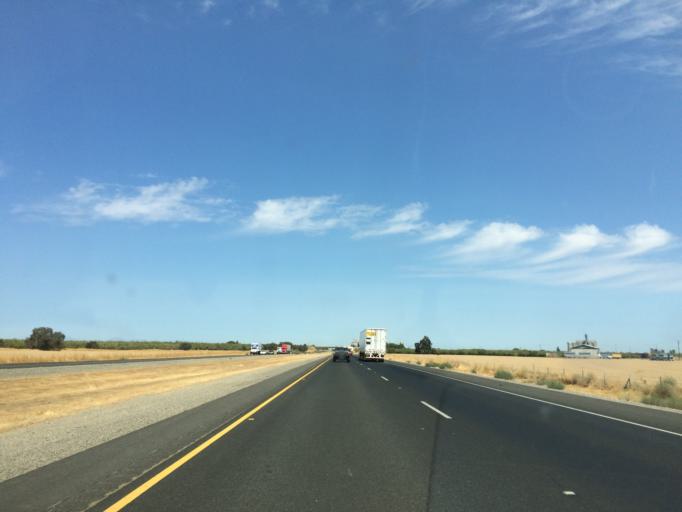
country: US
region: California
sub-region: Colusa County
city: Arbuckle
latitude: 38.9582
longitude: -122.0206
